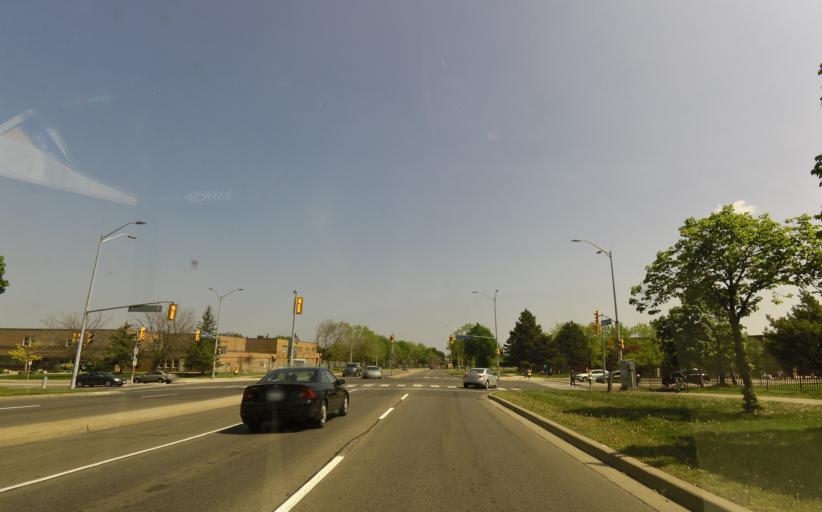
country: CA
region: Ontario
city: Mississauga
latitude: 43.5994
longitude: -79.6239
